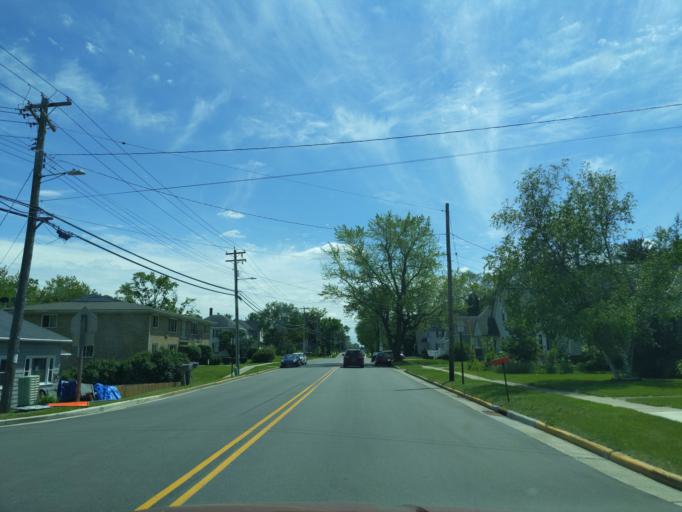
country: US
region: Wisconsin
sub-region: Columbia County
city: Pardeeville
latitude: 43.5338
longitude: -89.3012
